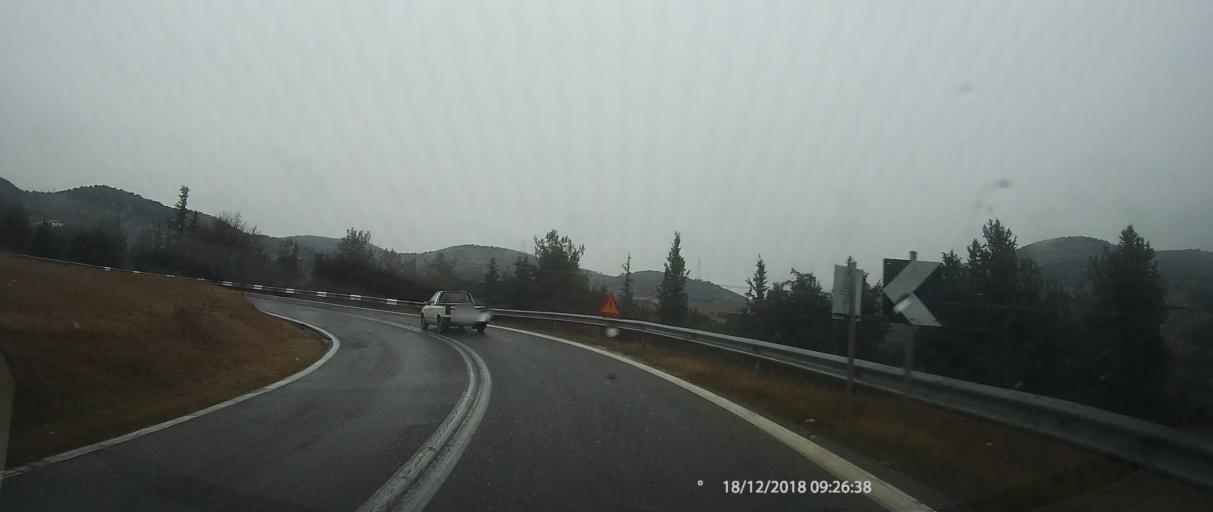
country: GR
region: Thessaly
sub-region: Nomos Larisis
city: Elassona
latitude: 39.9155
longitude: 22.1831
